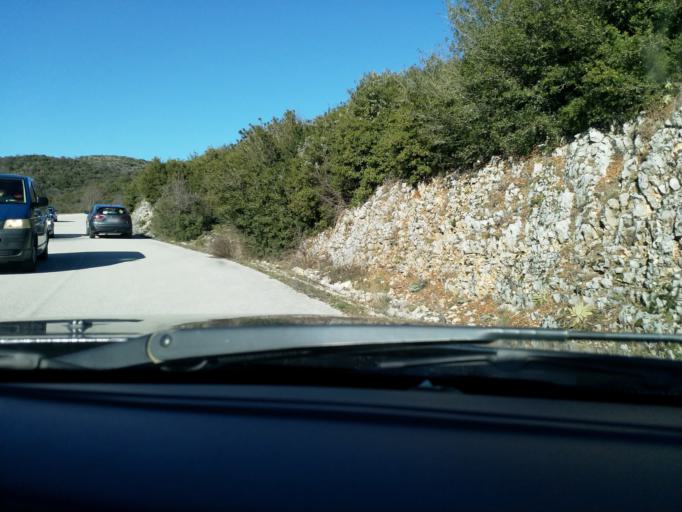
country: GR
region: Epirus
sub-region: Nomos Ioanninon
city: Kalpaki
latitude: 39.9028
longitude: 20.6726
